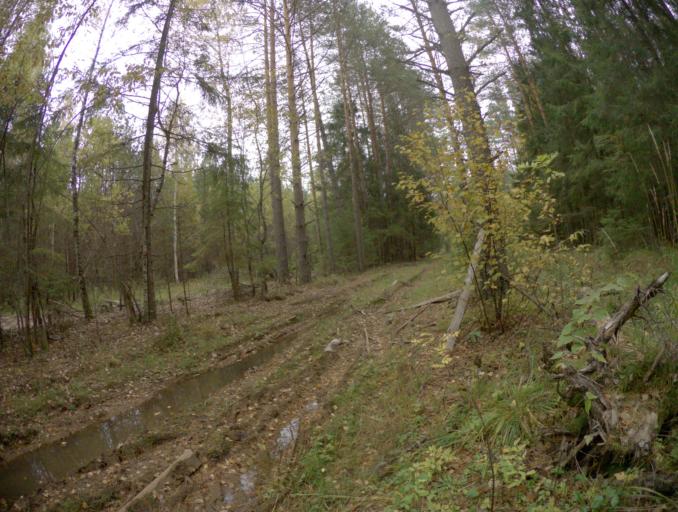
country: RU
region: Vladimir
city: Stepantsevo
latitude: 56.3137
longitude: 41.5912
